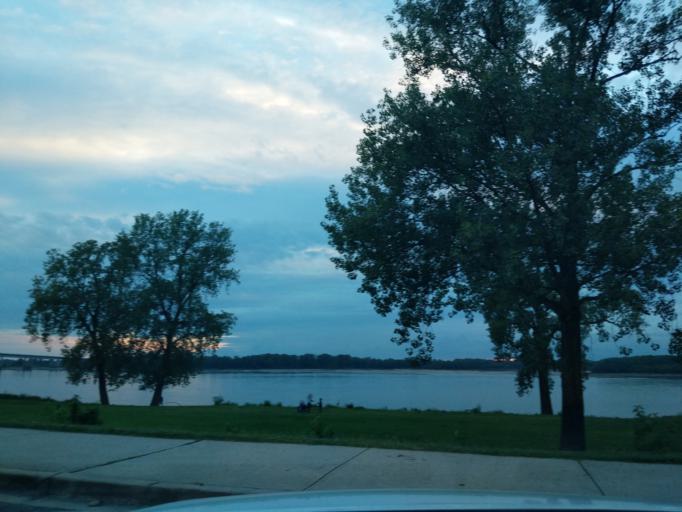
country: US
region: Tennessee
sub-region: Shelby County
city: Memphis
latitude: 35.1609
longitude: -90.0563
